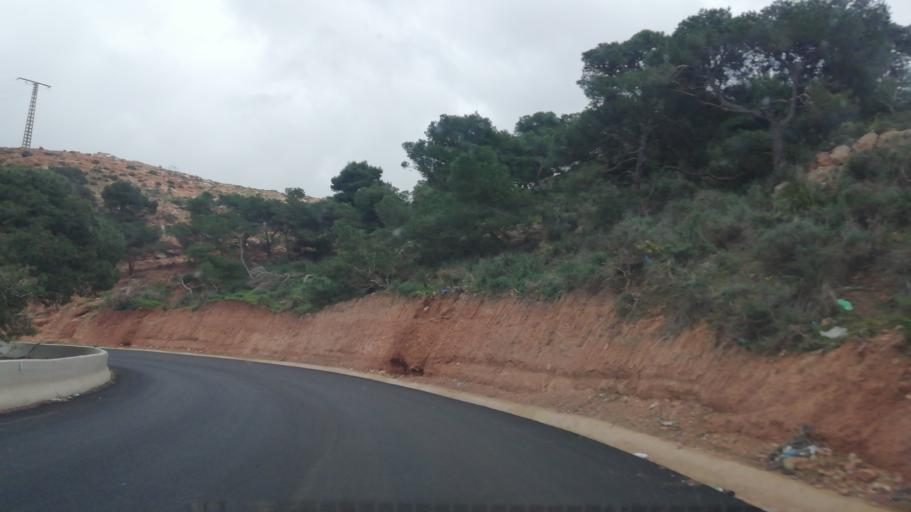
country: DZ
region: Oran
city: Bir el Djir
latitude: 35.7614
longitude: -0.5298
